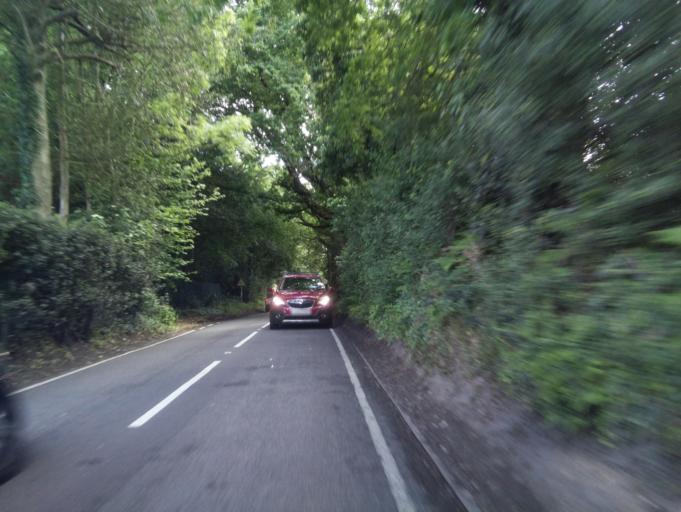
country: GB
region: England
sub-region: Hertfordshire
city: Chorleywood
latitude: 51.6720
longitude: -0.4617
